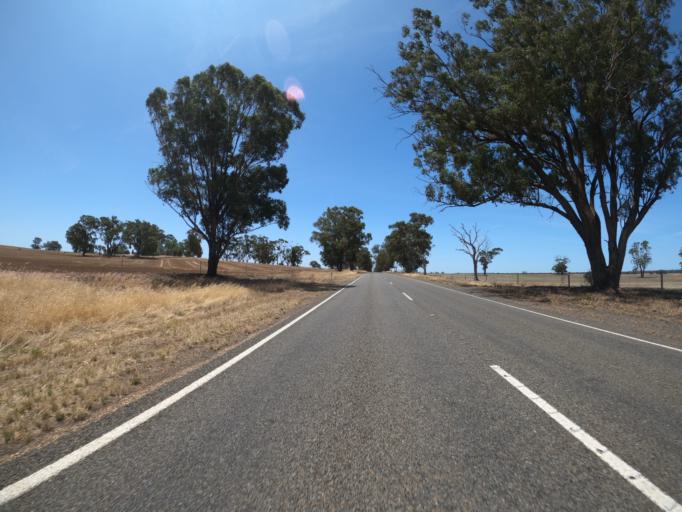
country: AU
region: Victoria
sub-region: Moira
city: Yarrawonga
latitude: -36.1057
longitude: 145.9885
